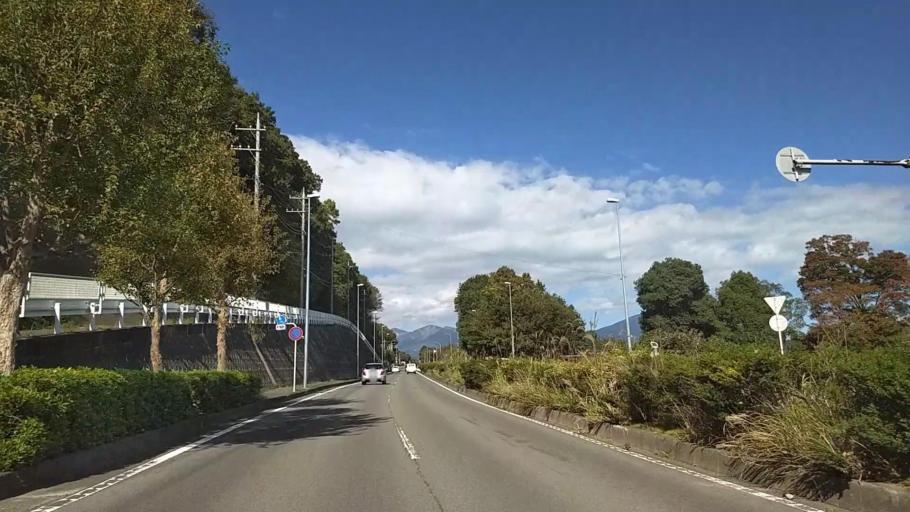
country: JP
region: Kanagawa
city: Ninomiya
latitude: 35.3289
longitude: 139.2327
